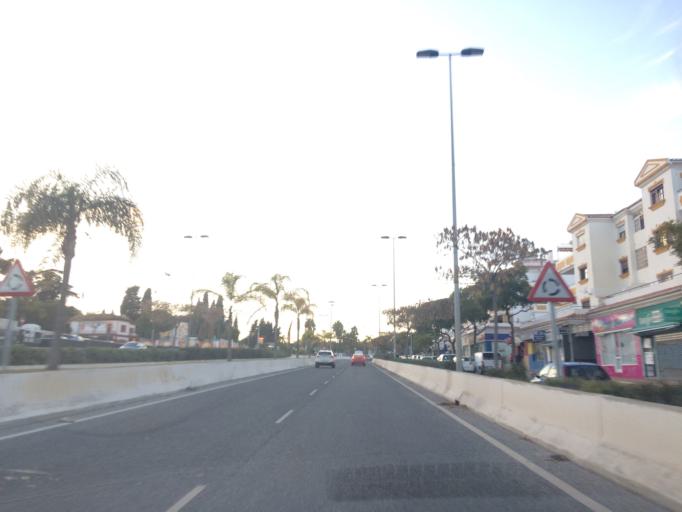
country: ES
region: Andalusia
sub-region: Provincia de Malaga
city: Torremolinos
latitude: 36.6616
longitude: -4.5038
